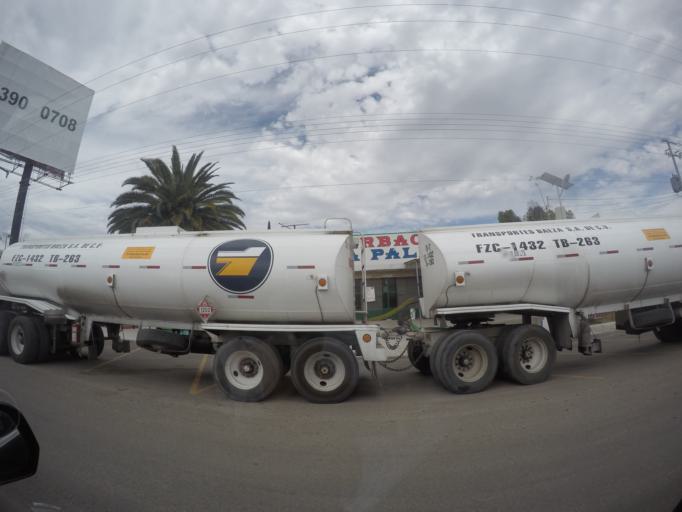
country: MX
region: Queretaro
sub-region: San Juan del Rio
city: Paso de Mata
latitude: 20.3348
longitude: -99.9396
